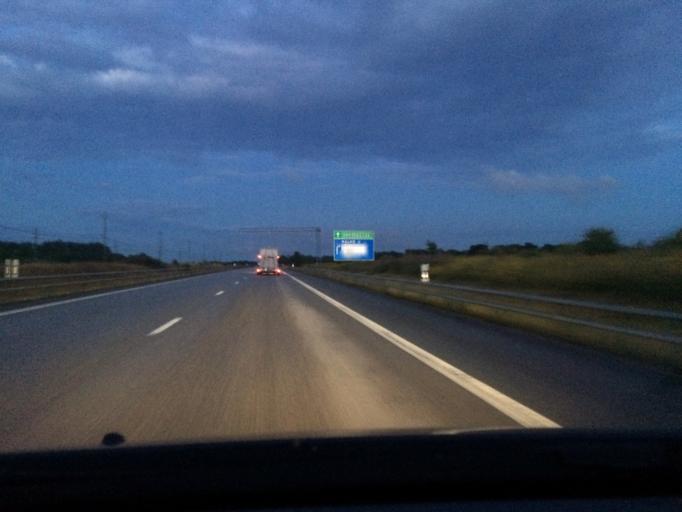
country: SE
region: Skane
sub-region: Malmo
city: Bunkeflostrand
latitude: 55.5566
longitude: 12.9421
